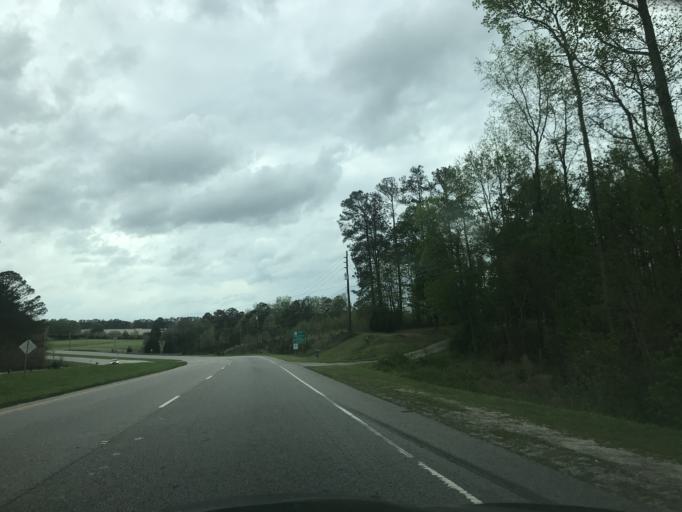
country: US
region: North Carolina
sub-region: Wake County
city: Knightdale
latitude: 35.8075
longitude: -78.4543
